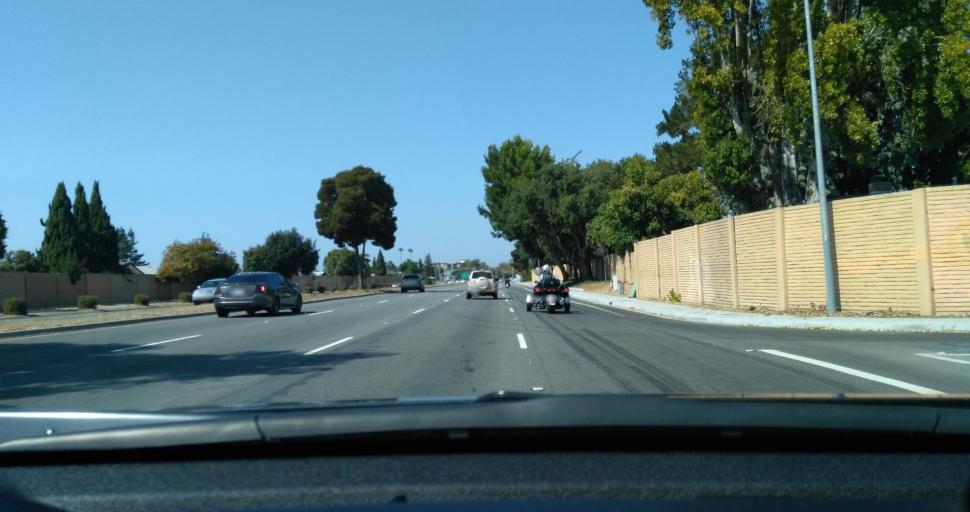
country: US
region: California
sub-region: Santa Clara County
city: Sunnyvale
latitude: 37.3993
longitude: -121.9956
